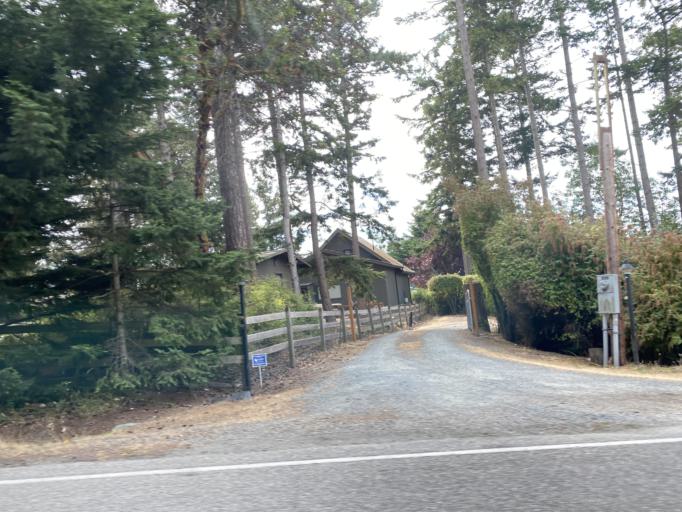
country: US
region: Washington
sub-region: Island County
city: Coupeville
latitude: 48.2393
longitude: -122.7080
